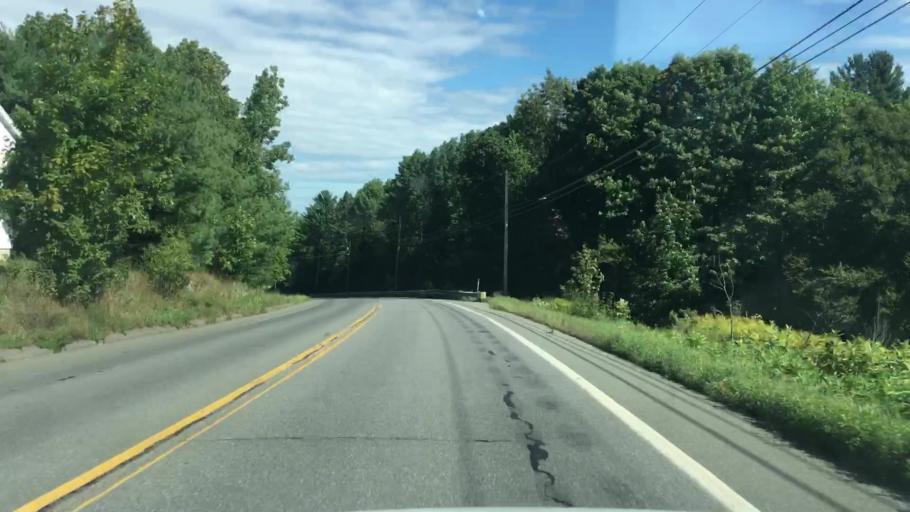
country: US
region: Maine
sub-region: Penobscot County
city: Dexter
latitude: 45.0758
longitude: -69.2320
